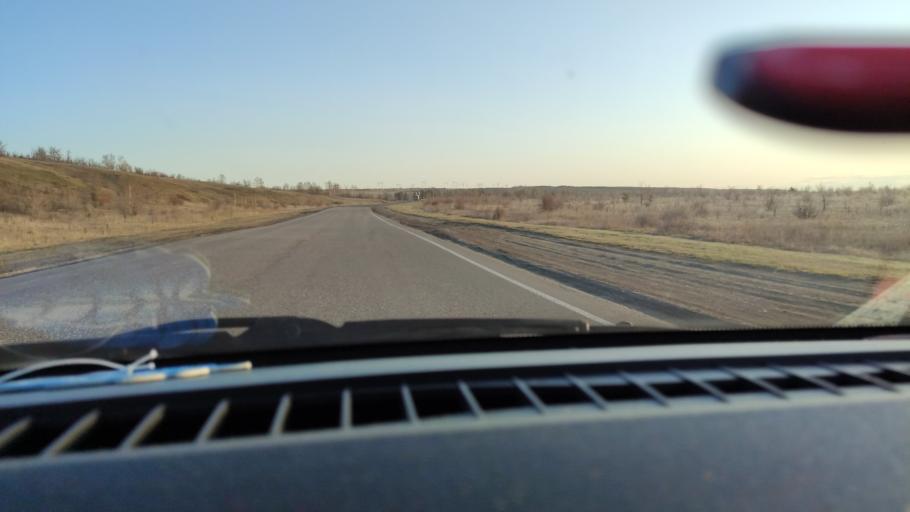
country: RU
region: Saratov
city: Sennoy
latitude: 52.0958
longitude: 46.8125
